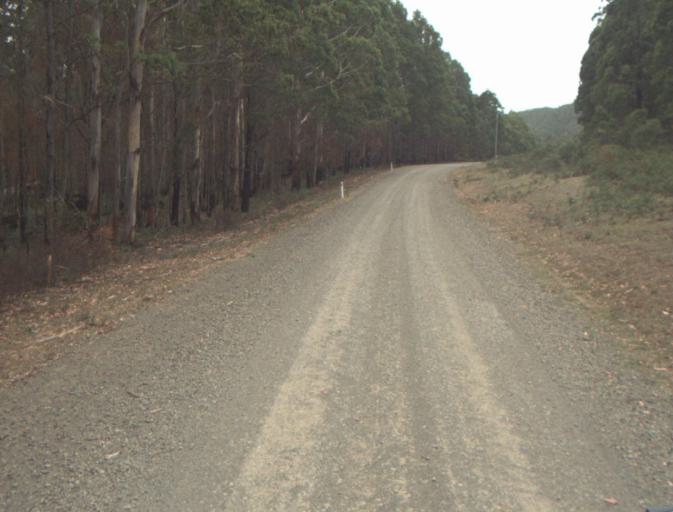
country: AU
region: Tasmania
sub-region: Dorset
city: Scottsdale
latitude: -41.4330
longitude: 147.5150
